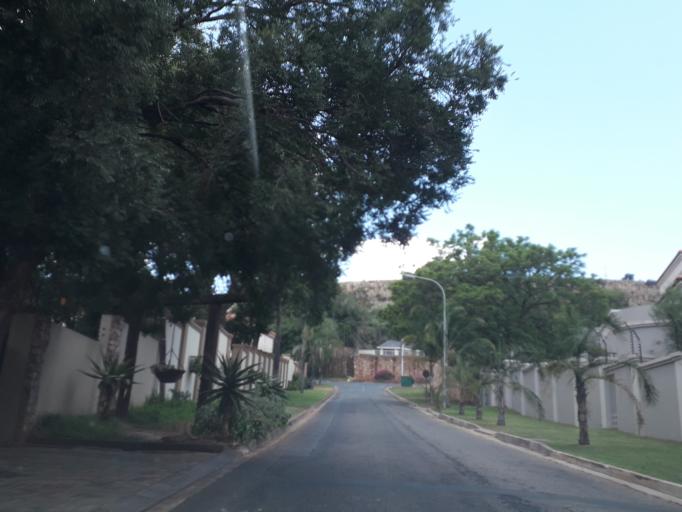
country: ZA
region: Gauteng
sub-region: City of Johannesburg Metropolitan Municipality
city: Roodepoort
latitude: -26.1381
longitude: 27.9648
